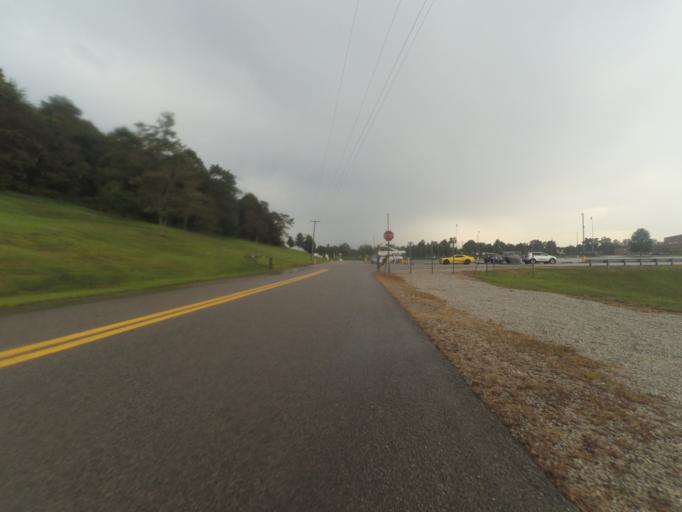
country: US
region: West Virginia
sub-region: Cabell County
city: Huntington
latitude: 38.3942
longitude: -82.3954
